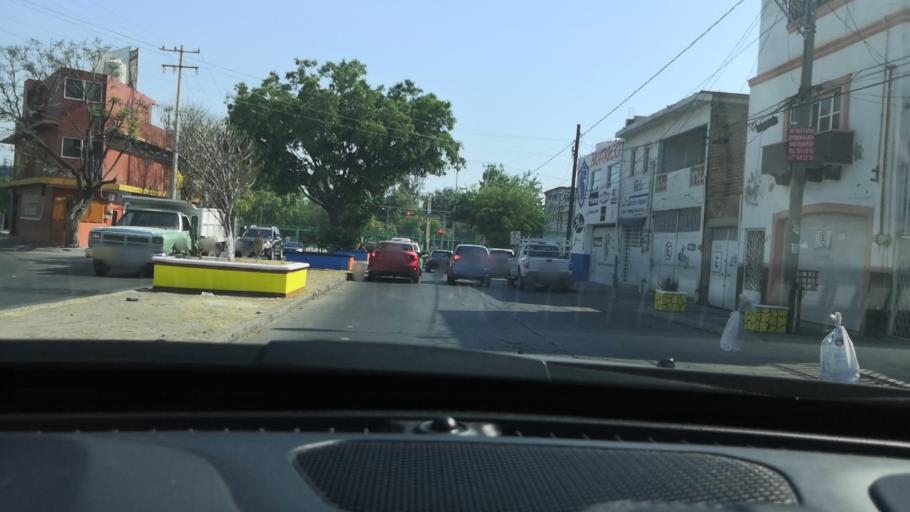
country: MX
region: Guanajuato
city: Leon
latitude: 21.1055
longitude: -101.7032
